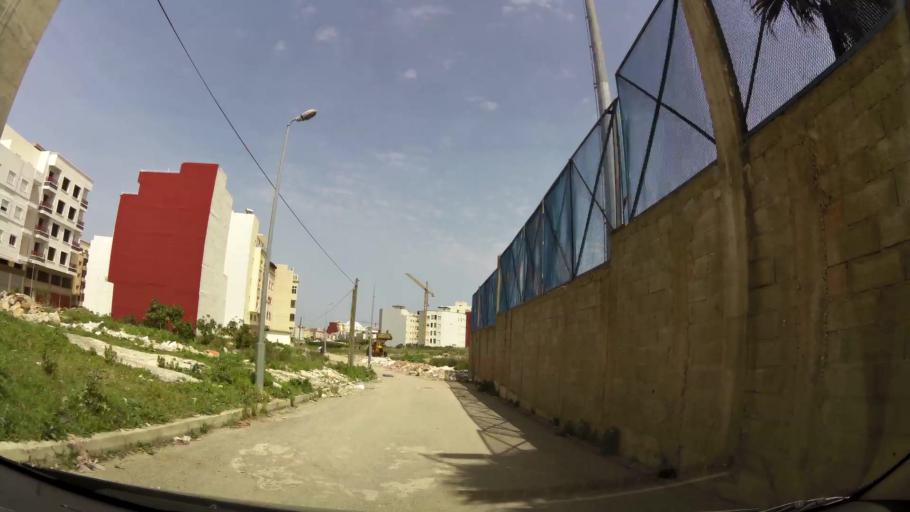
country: MA
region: Tanger-Tetouan
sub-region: Tanger-Assilah
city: Tangier
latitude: 35.7471
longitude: -5.8453
